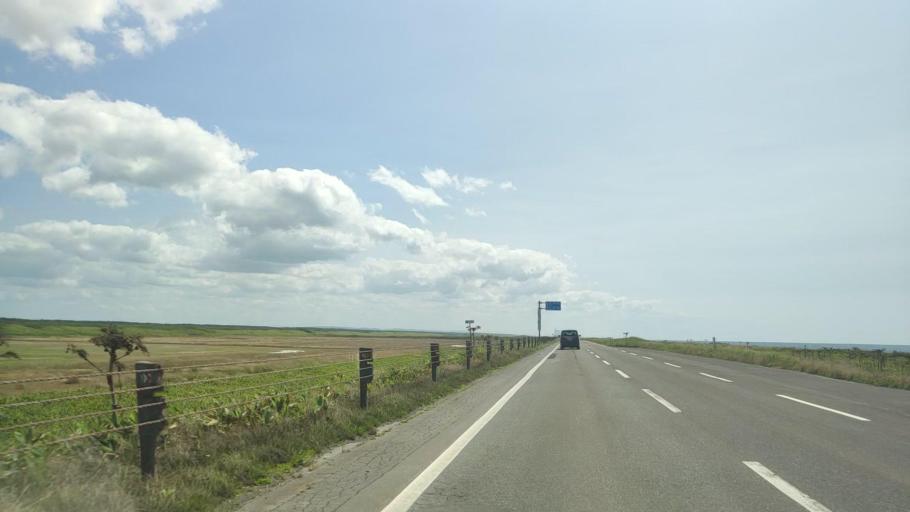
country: JP
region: Hokkaido
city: Wakkanai
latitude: 45.0443
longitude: 141.6569
